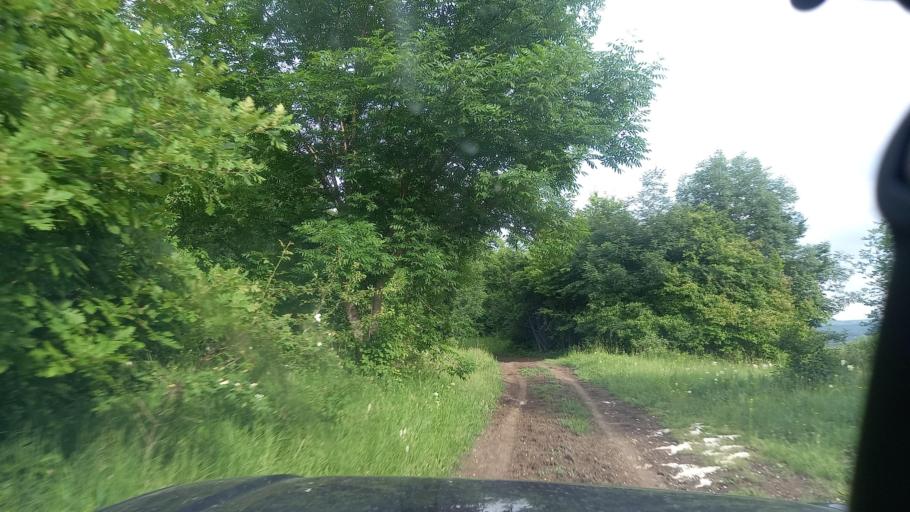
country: RU
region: Karachayevo-Cherkesiya
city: Kurdzhinovo
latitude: 44.1256
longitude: 41.0801
